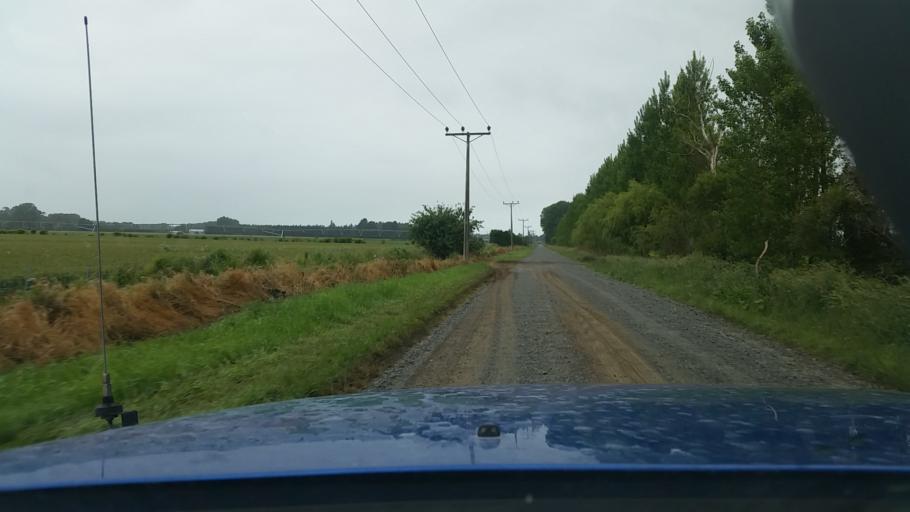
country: NZ
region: Canterbury
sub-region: Ashburton District
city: Tinwald
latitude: -44.0026
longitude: 171.6712
